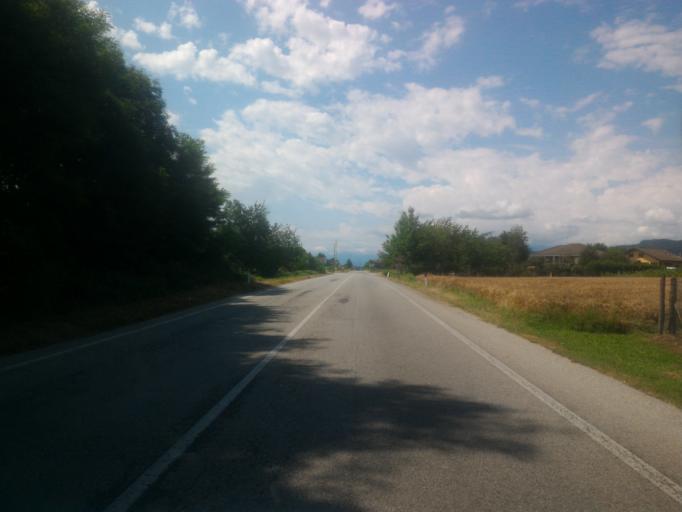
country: IT
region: Piedmont
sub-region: Provincia di Torino
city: Frossasco
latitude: 44.9368
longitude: 7.3722
